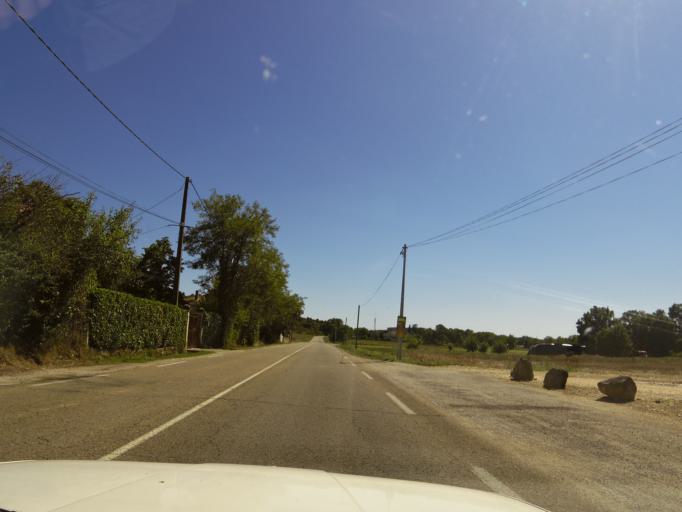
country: FR
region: Languedoc-Roussillon
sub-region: Departement du Gard
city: Saint-Hilaire-de-Brethmas
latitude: 44.0750
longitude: 4.1175
